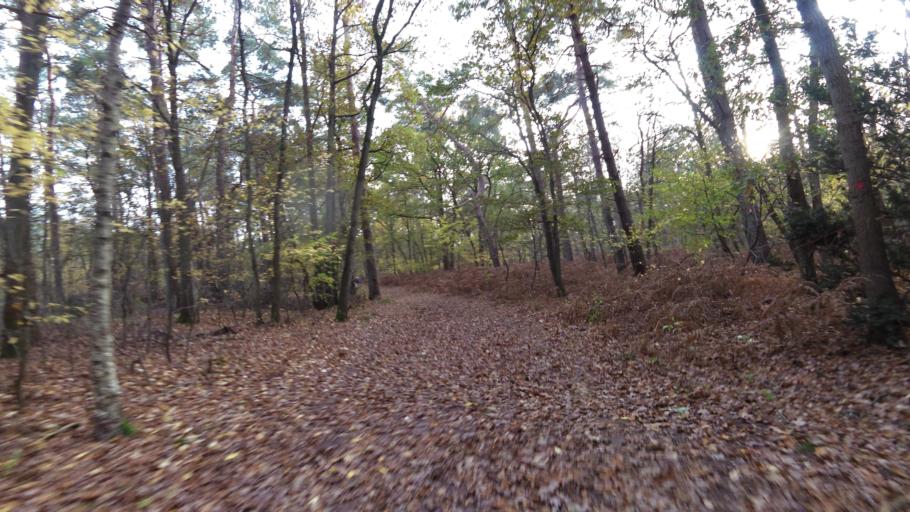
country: NL
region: North Holland
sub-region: Gemeente Hilversum
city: Hilversum
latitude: 52.1940
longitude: 5.1838
